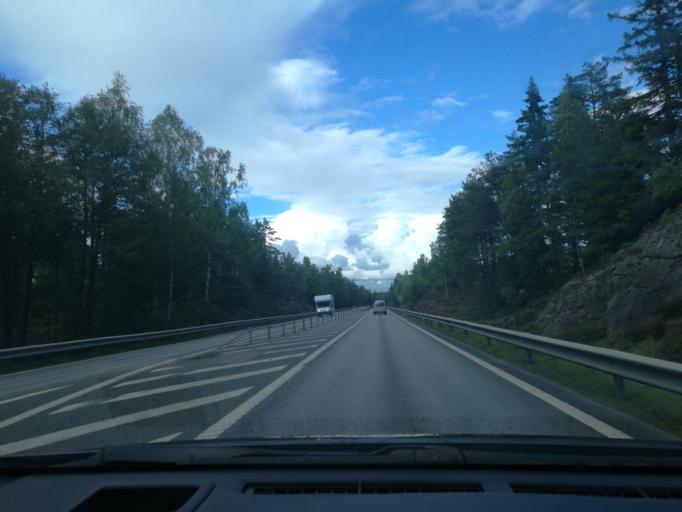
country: SE
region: OEstergoetland
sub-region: Norrkopings Kommun
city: Jursla
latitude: 58.7112
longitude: 16.1614
